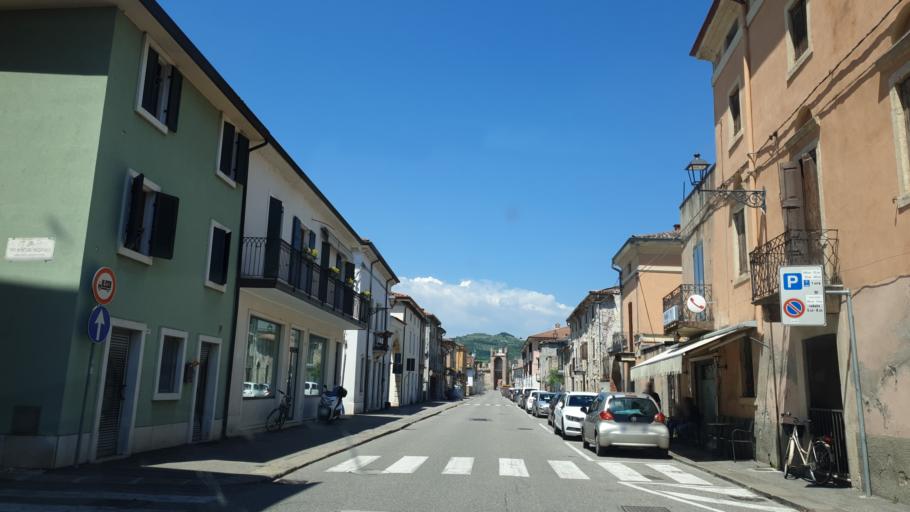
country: IT
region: Veneto
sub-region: Provincia di Verona
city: Soave
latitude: 45.4212
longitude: 11.2471
